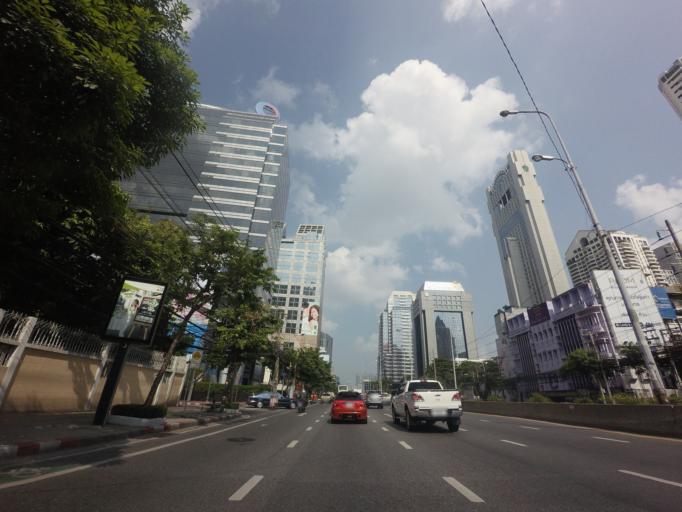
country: TH
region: Bangkok
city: Bang Rak
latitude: 13.7242
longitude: 100.5376
